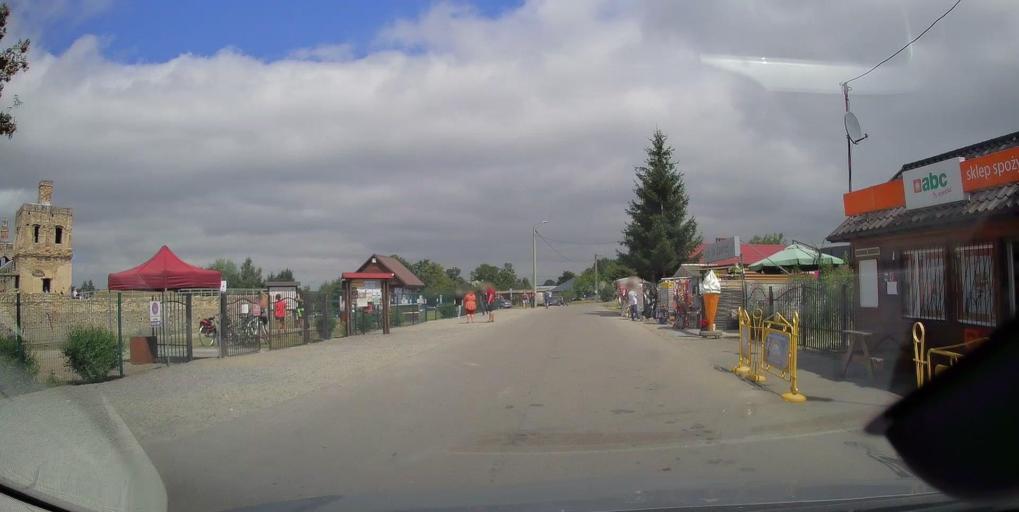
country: PL
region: Swietokrzyskie
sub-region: Powiat opatowski
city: Iwaniska
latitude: 50.7133
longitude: 21.3113
